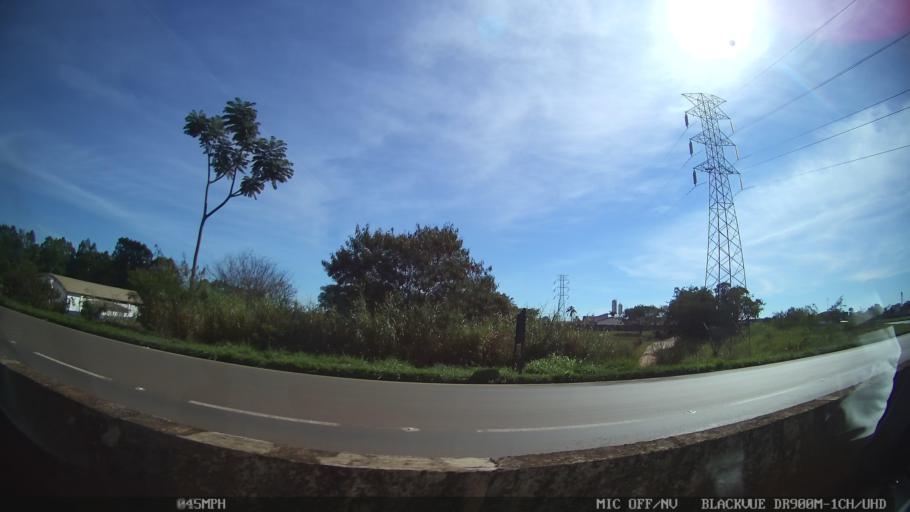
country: BR
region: Sao Paulo
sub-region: Pirassununga
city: Pirassununga
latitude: -22.0389
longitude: -47.4338
